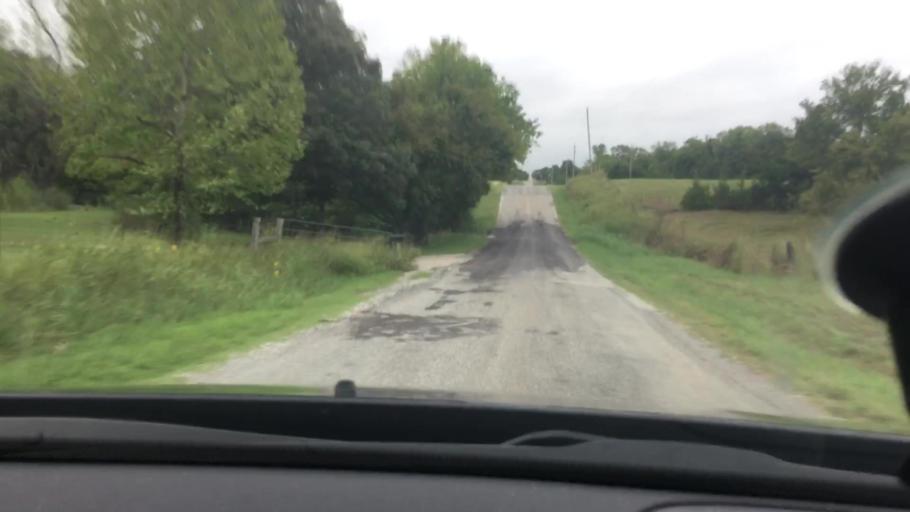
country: US
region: Oklahoma
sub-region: Pontotoc County
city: Byng
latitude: 34.8052
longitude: -96.5475
